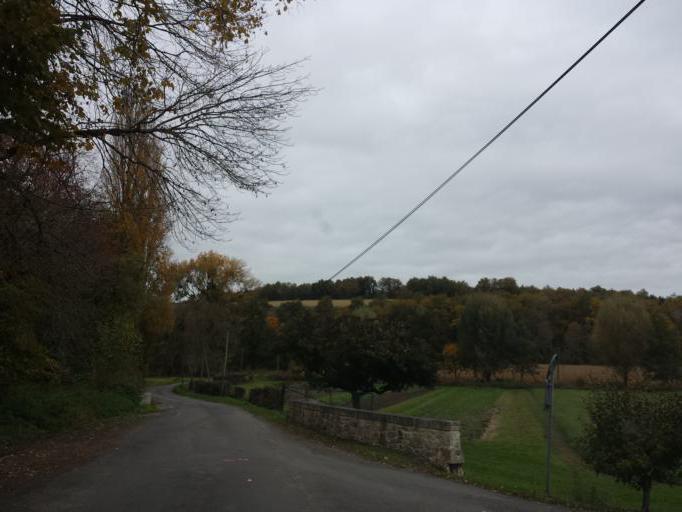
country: FR
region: Poitou-Charentes
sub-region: Departement de la Charente
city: Puymoyen
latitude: 45.6038
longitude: 0.1790
